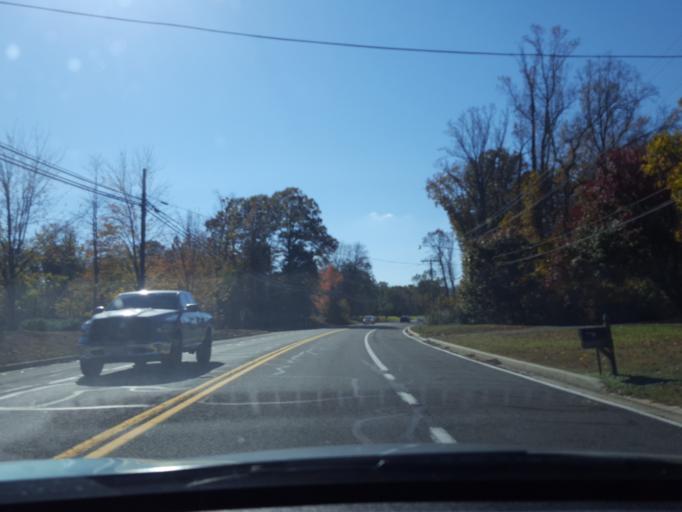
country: US
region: Maryland
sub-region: Calvert County
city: Chesapeake Ranch Estates
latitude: 38.3564
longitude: -76.4519
